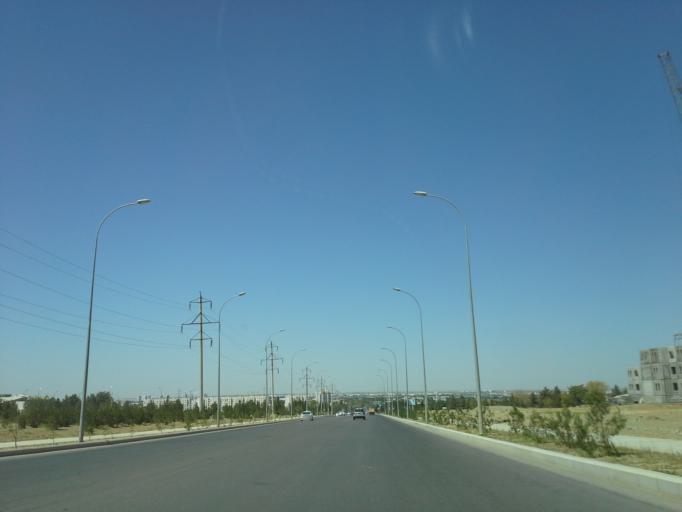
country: TM
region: Ahal
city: Ashgabat
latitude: 37.8971
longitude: 58.4057
